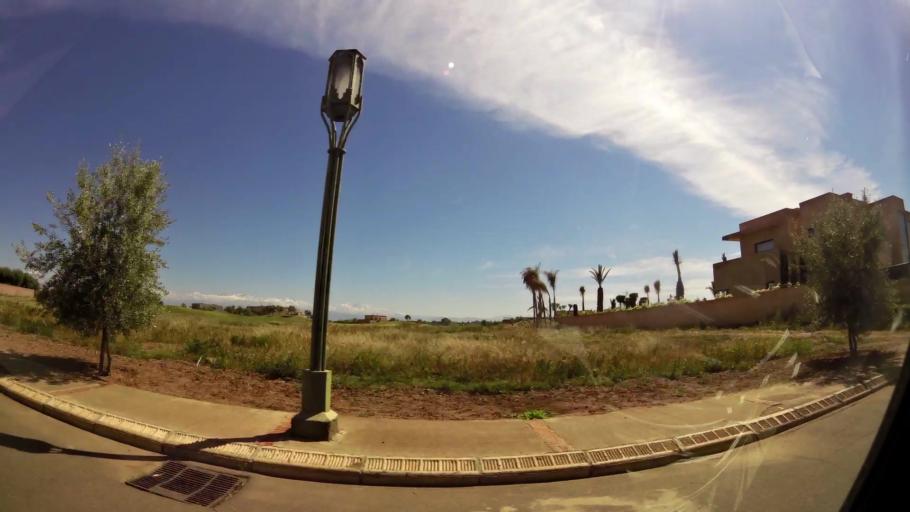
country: MA
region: Marrakech-Tensift-Al Haouz
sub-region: Marrakech
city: Marrakesh
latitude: 31.6216
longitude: -7.9246
